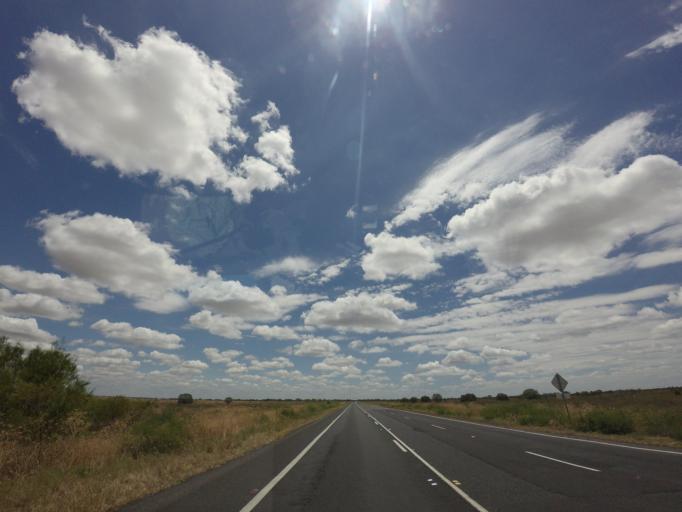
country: AU
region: New South Wales
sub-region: Moree Plains
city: Boggabilla
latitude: -28.9416
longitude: 150.0998
